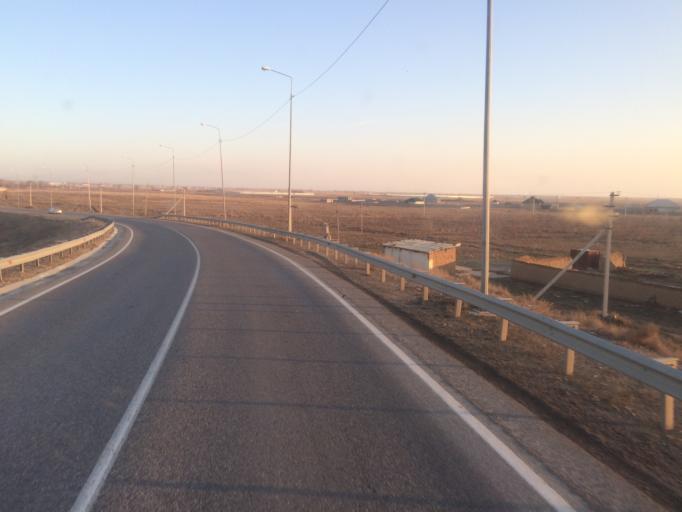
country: KZ
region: Ongtustik Qazaqstan
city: Turkestan
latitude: 43.2742
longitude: 68.3363
